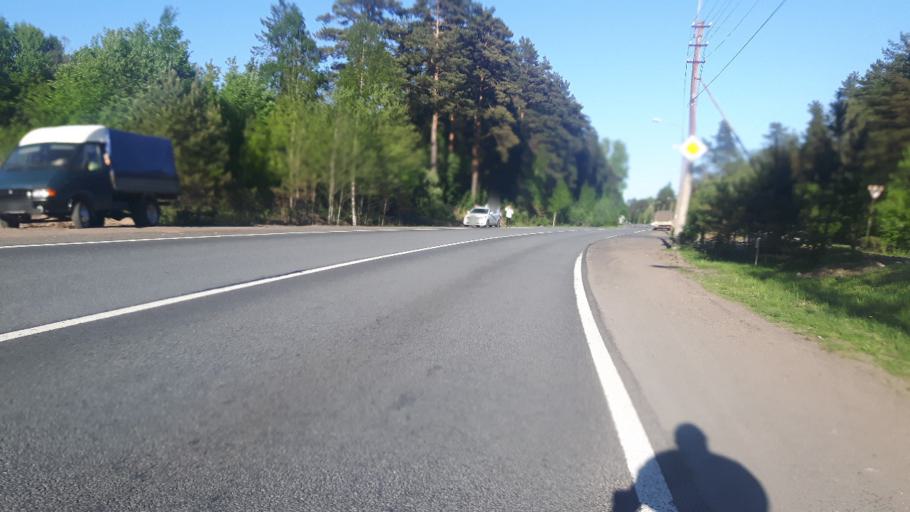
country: RU
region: Leningrad
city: Molodezhnoye
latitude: 60.1805
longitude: 29.4549
